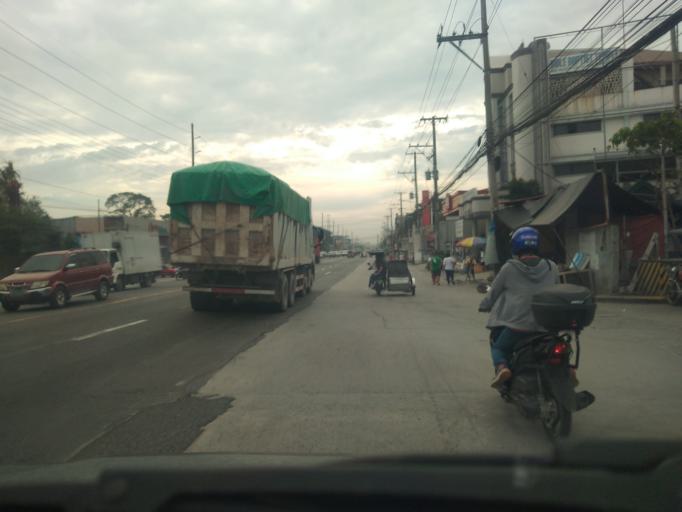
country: PH
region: Central Luzon
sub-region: Province of Pampanga
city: Magliman
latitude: 15.0484
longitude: 120.6671
